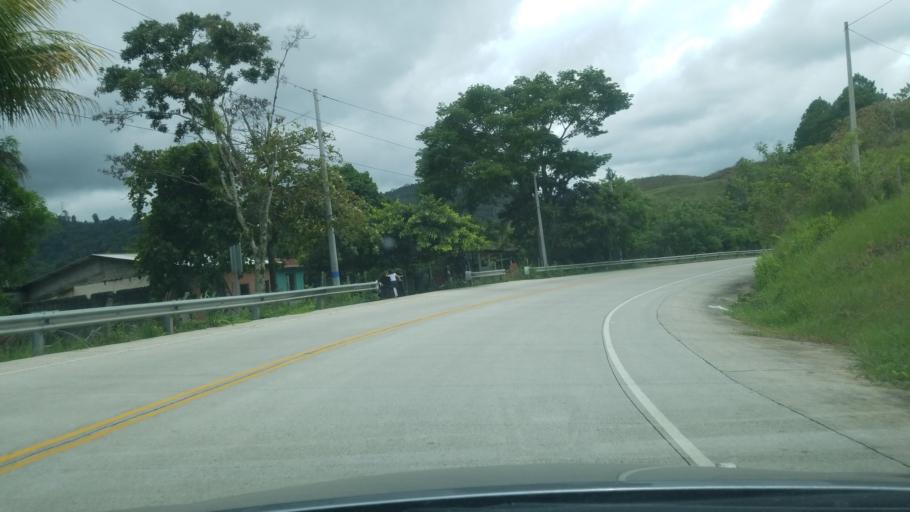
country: HN
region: Copan
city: San Jeronimo
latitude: 14.9338
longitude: -88.9316
